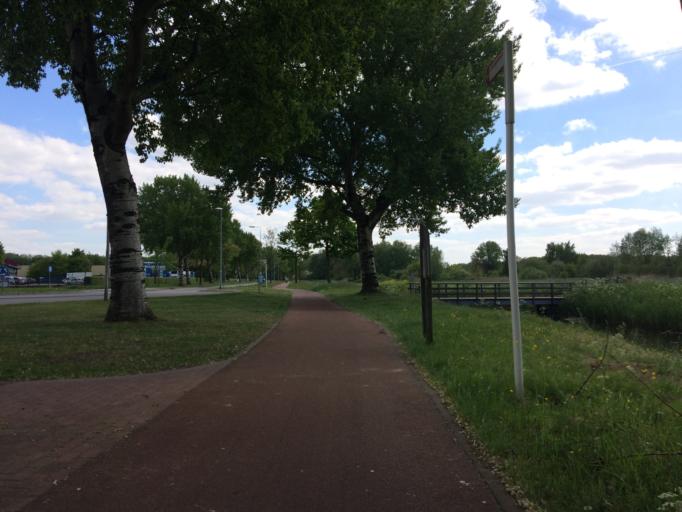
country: NL
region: Gelderland
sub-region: Gemeente Maasdriel
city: Hedel
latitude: 51.7147
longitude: 5.2585
